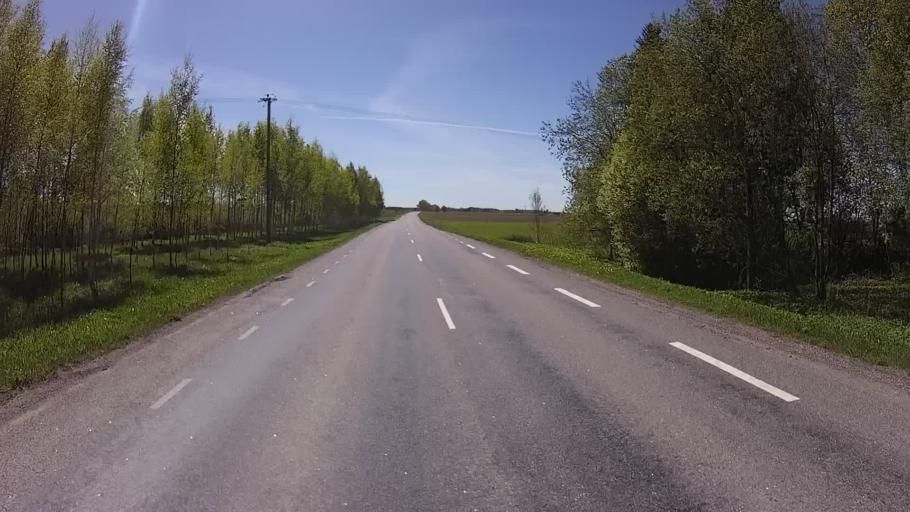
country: EE
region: Raplamaa
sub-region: Kehtna vald
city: Kehtna
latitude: 59.0558
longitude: 25.1366
